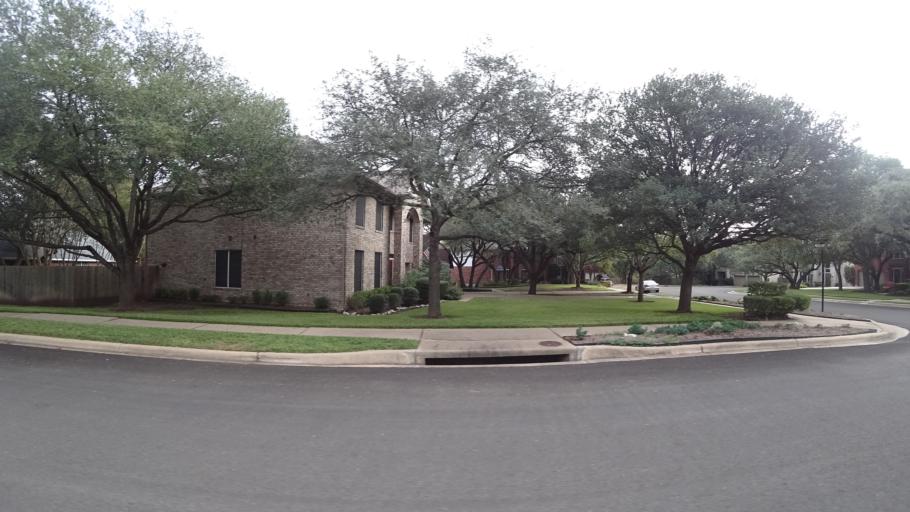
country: US
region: Texas
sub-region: Travis County
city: Shady Hollow
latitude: 30.1907
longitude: -97.8852
